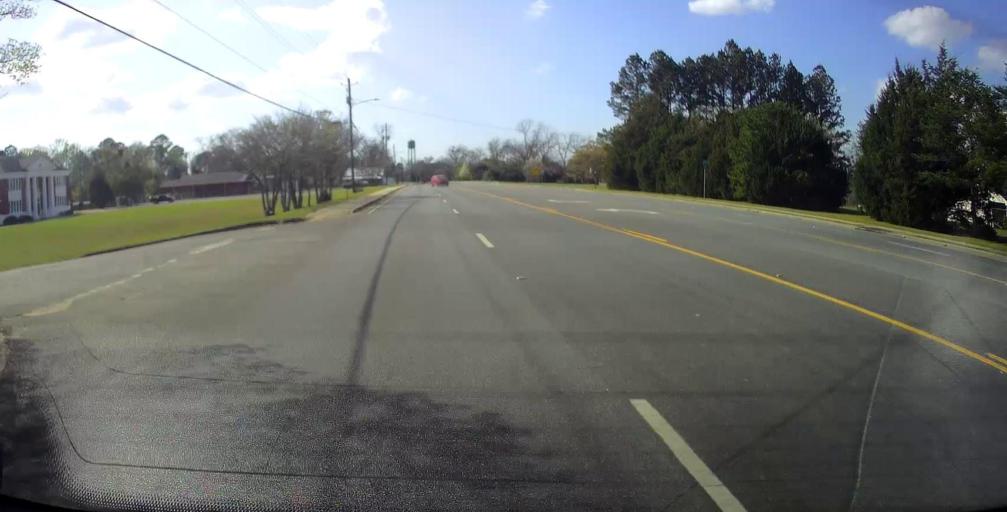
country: US
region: Georgia
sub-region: Telfair County
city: Helena
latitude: 32.1032
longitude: -83.0593
